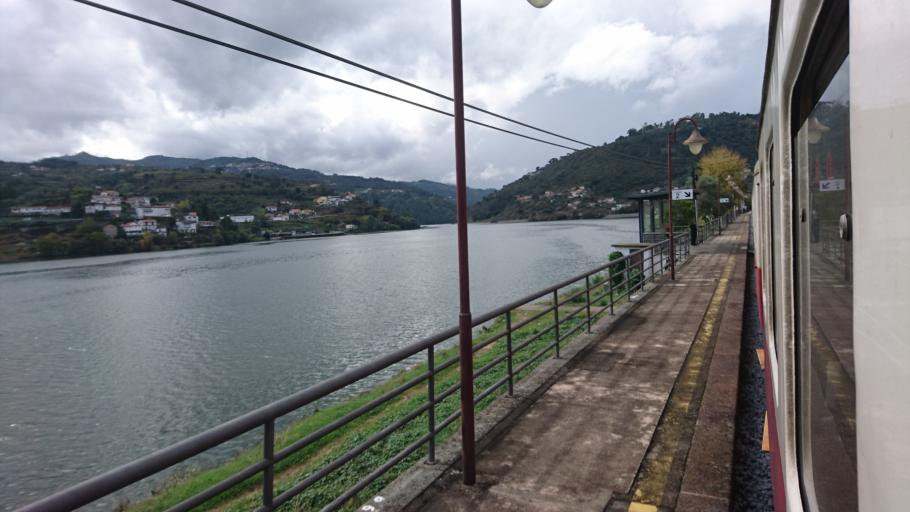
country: PT
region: Viseu
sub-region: Resende
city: Resende
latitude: 41.1064
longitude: -8.0070
